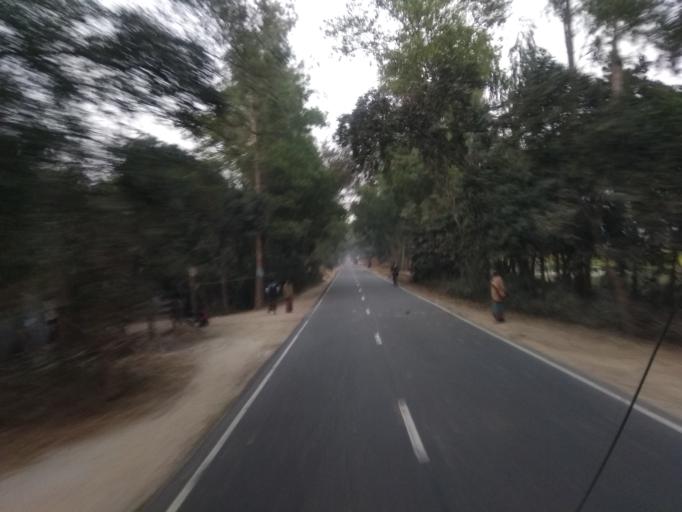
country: BD
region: Rajshahi
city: Bogra
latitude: 24.6635
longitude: 89.2705
